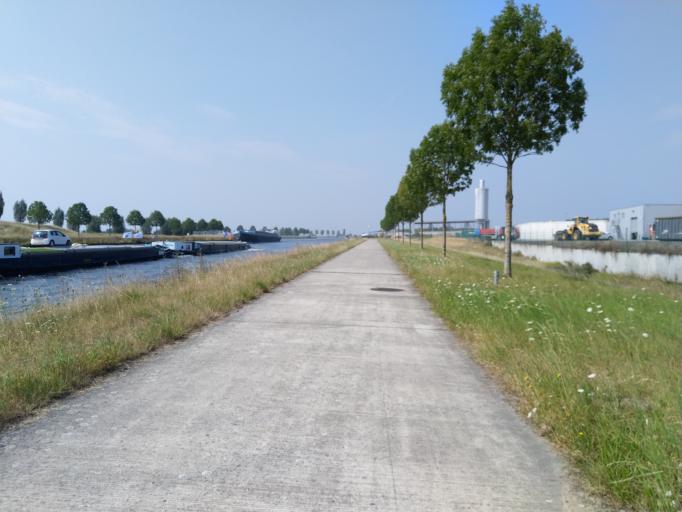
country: BE
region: Wallonia
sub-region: Province du Hainaut
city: Roeulx
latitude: 50.4903
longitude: 4.1272
